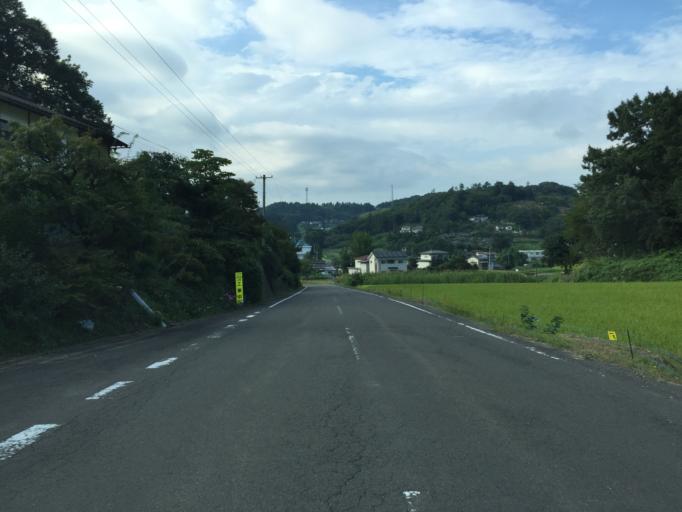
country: JP
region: Fukushima
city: Fukushima-shi
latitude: 37.6619
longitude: 140.5494
